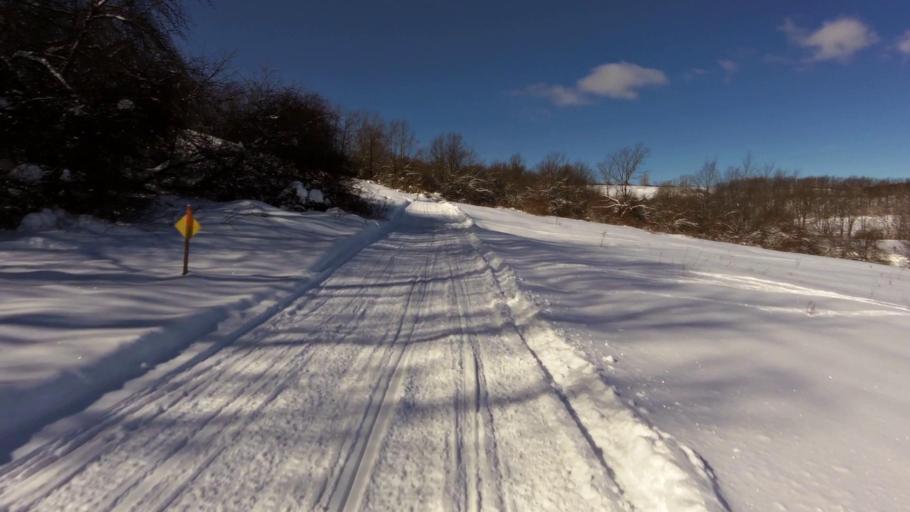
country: US
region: New York
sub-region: Chautauqua County
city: Fredonia
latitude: 42.3562
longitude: -79.1855
